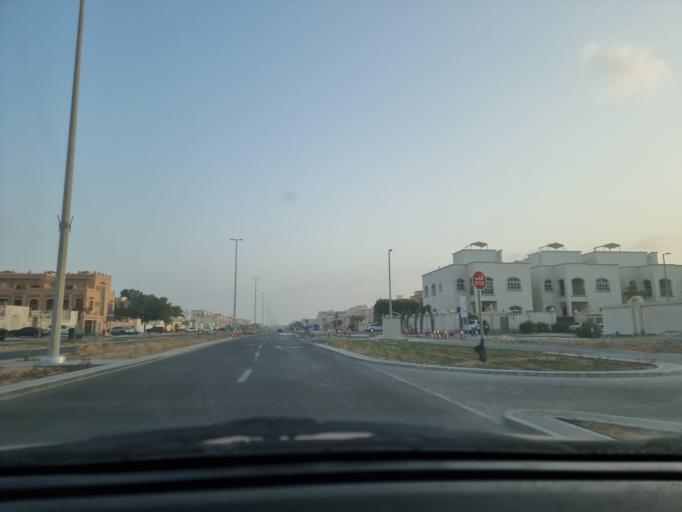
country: AE
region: Abu Dhabi
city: Abu Dhabi
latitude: 24.4257
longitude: 54.5733
